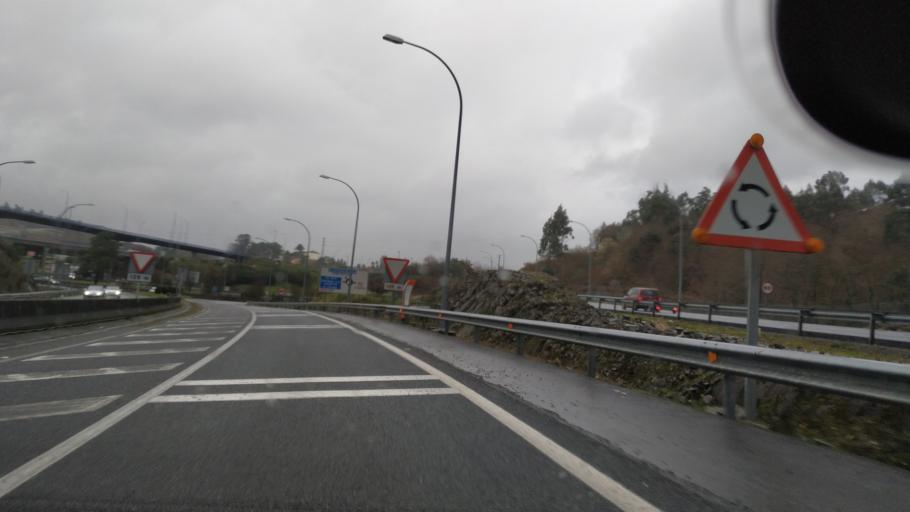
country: ES
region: Galicia
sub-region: Provincia da Coruna
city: Santiago de Compostela
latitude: 42.8533
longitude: -8.5308
